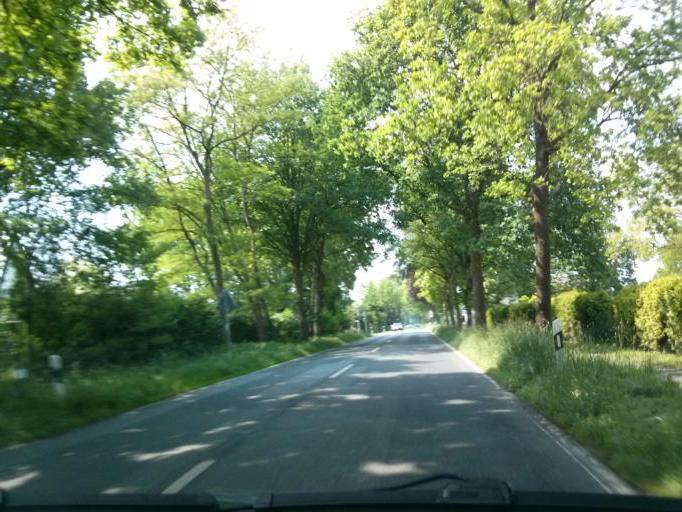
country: DE
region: Lower Saxony
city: Schiffdorf
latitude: 53.5204
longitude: 8.6721
